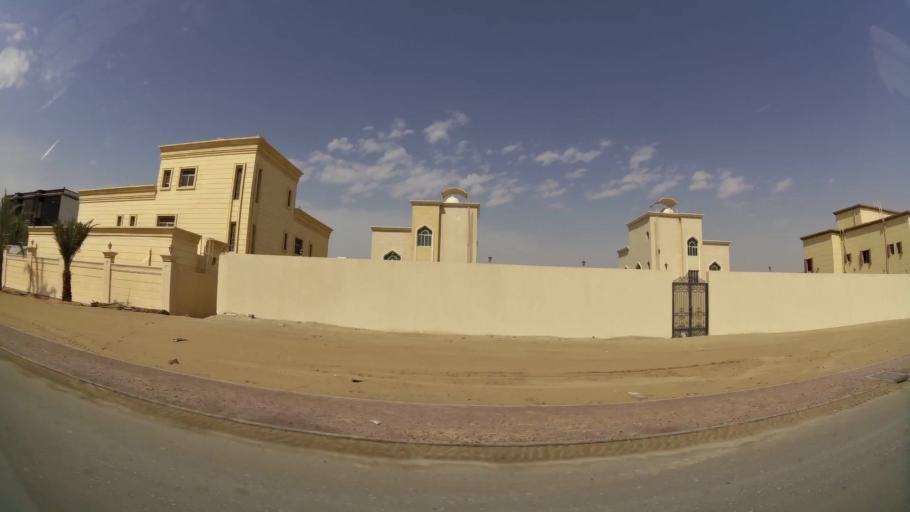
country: AE
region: Abu Dhabi
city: Abu Dhabi
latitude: 24.3154
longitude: 54.5428
